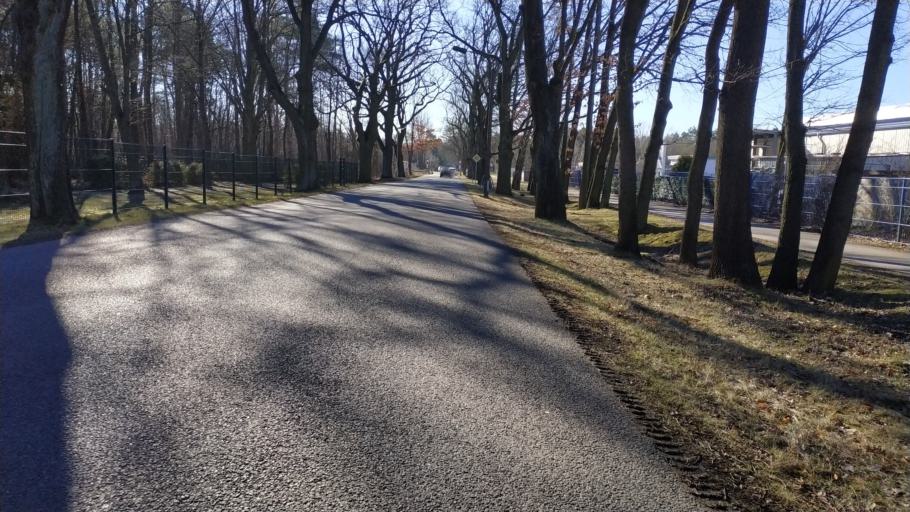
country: DE
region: Brandenburg
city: Petershagen
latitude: 52.5323
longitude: 13.8108
